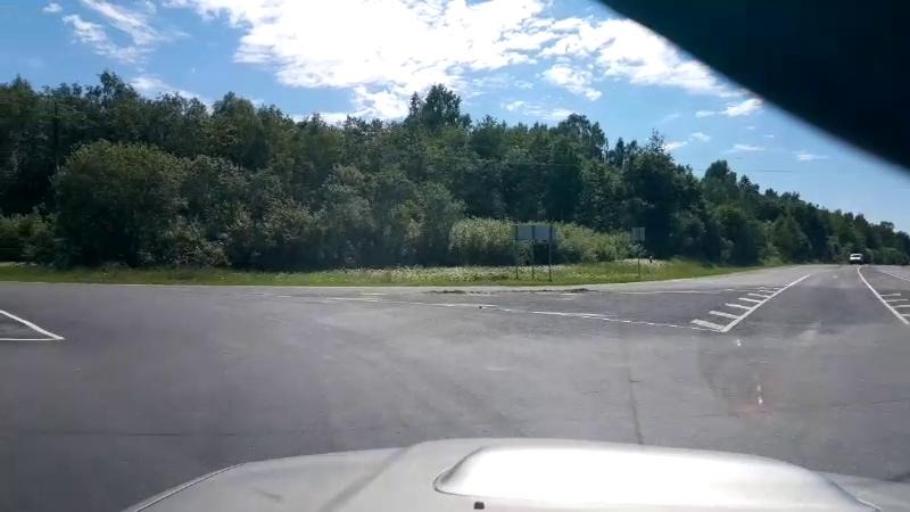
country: EE
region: Jaervamaa
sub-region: Jaerva-Jaani vald
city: Jarva-Jaani
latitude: 59.0481
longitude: 25.8781
